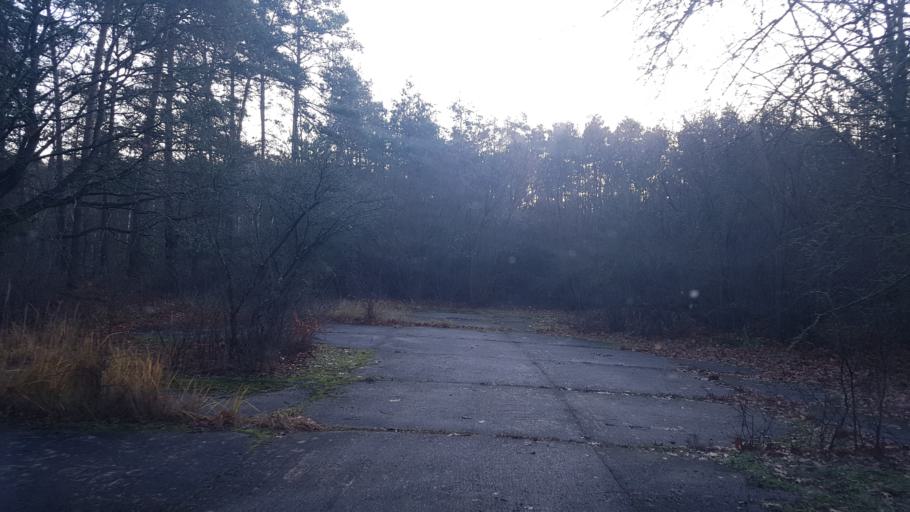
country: DE
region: Brandenburg
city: Ruckersdorf
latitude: 51.5896
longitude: 13.5878
